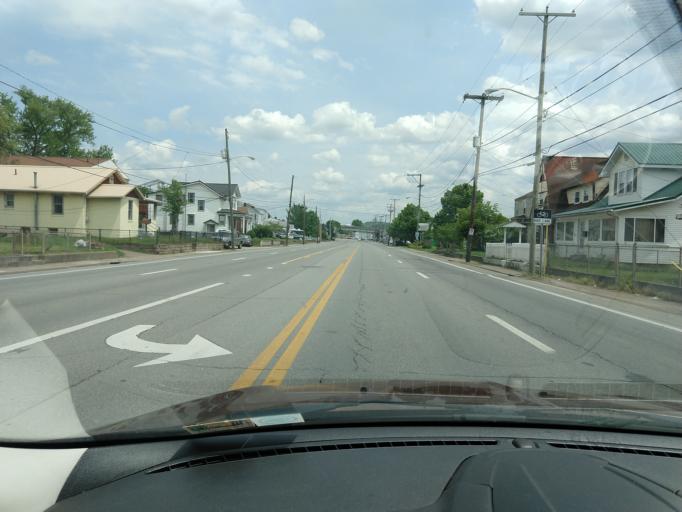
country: US
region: West Virginia
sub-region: Kanawha County
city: Dunbar
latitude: 38.3538
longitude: -81.7400
